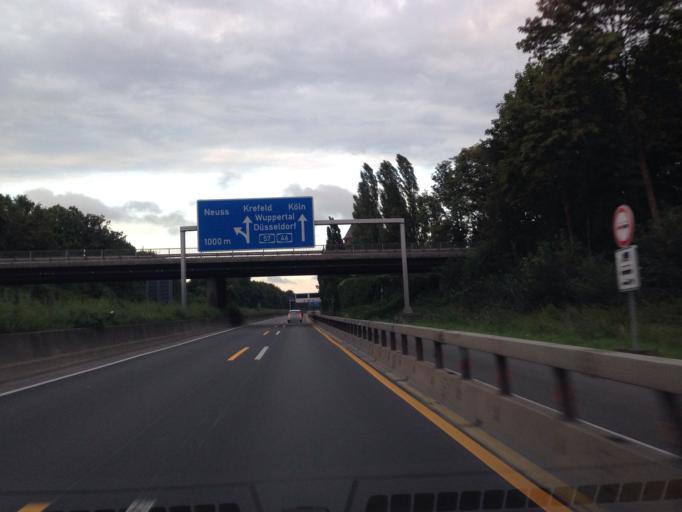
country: DE
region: North Rhine-Westphalia
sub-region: Regierungsbezirk Dusseldorf
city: Neubrueck
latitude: 51.1686
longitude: 6.6534
